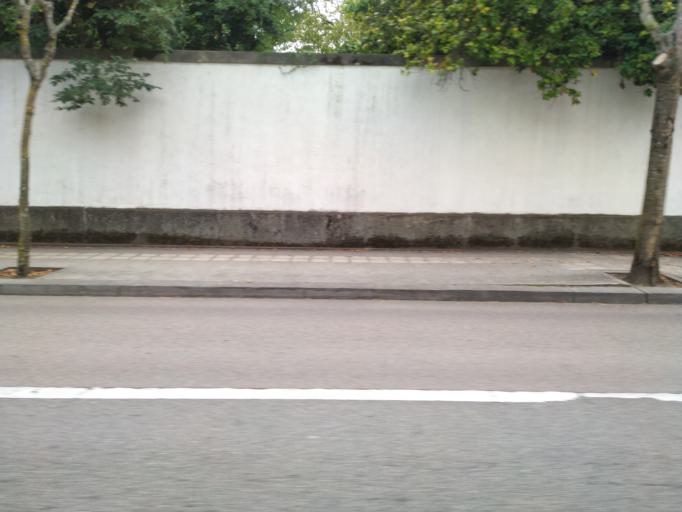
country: PT
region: Porto
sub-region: Porto
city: Porto
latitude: 41.1532
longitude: -8.6392
